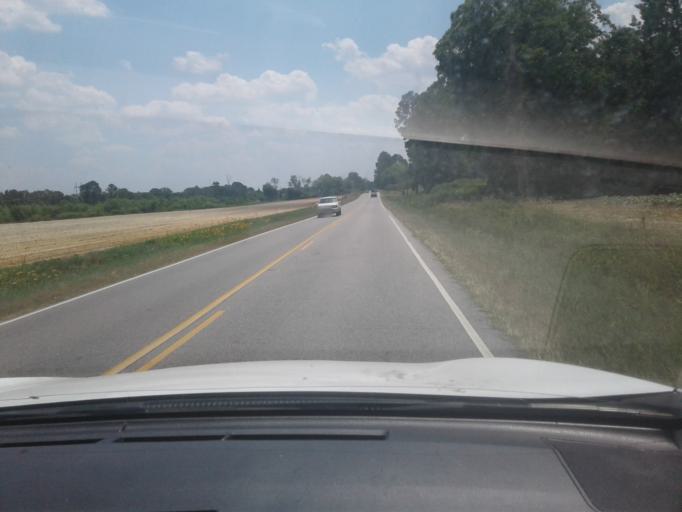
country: US
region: North Carolina
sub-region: Harnett County
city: Erwin
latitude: 35.3485
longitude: -78.6411
